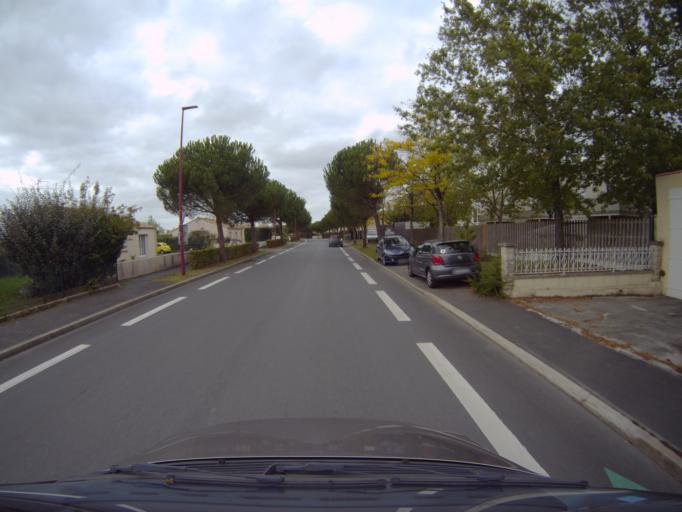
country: FR
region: Pays de la Loire
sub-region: Departement de la Loire-Atlantique
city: Clisson
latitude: 47.0915
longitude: -1.2708
